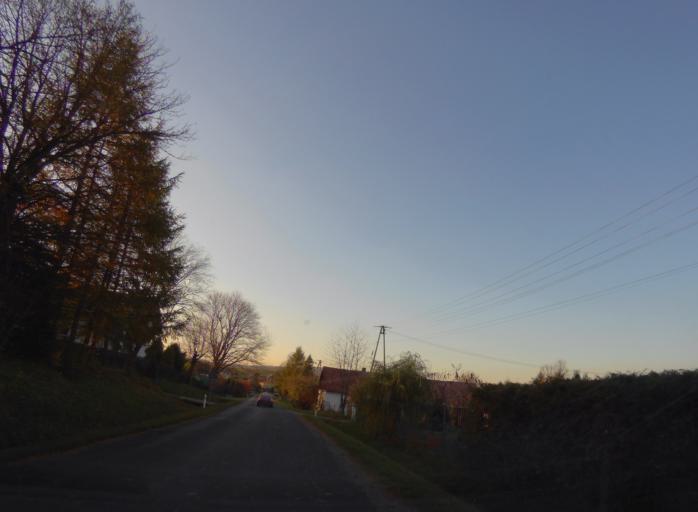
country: PL
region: Subcarpathian Voivodeship
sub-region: Powiat leski
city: Uherce Mineralne
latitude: 49.4069
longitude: 22.3610
